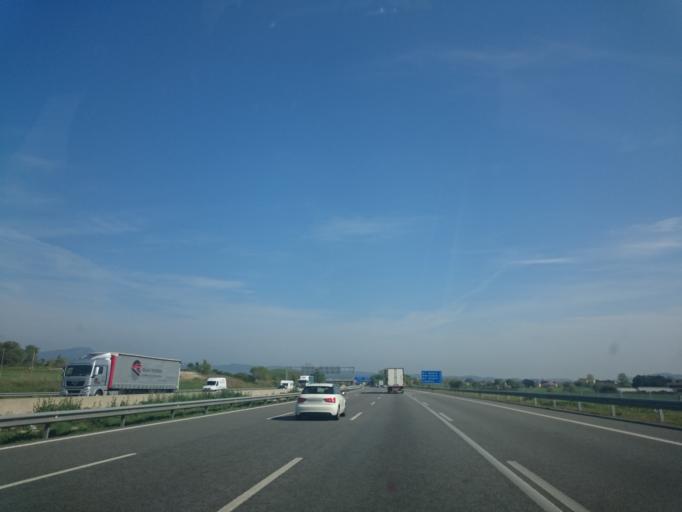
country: ES
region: Catalonia
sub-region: Provincia de Girona
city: Vilablareix
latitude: 41.9415
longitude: 2.7890
